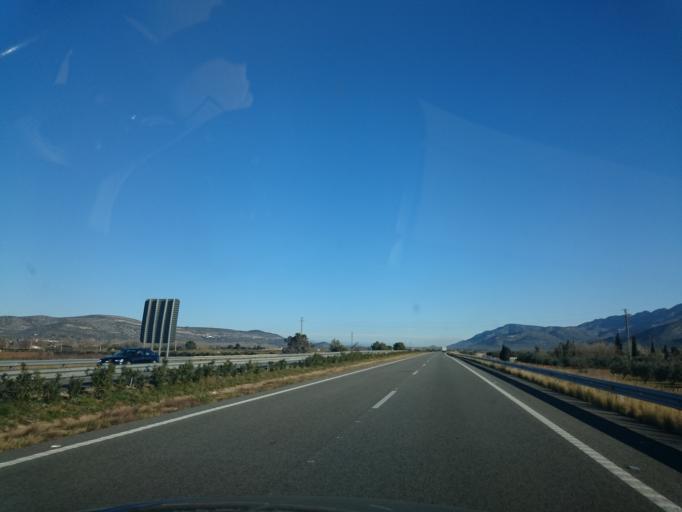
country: ES
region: Catalonia
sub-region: Provincia de Tarragona
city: Ulldecona
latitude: 40.5832
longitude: 0.4562
